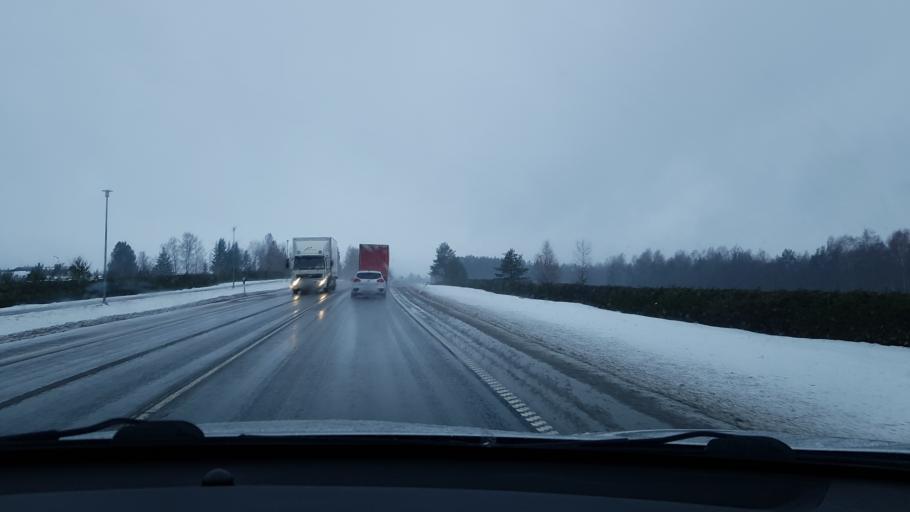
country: EE
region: Jaervamaa
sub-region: Tueri vald
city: Tueri
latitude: 58.8409
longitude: 25.4753
